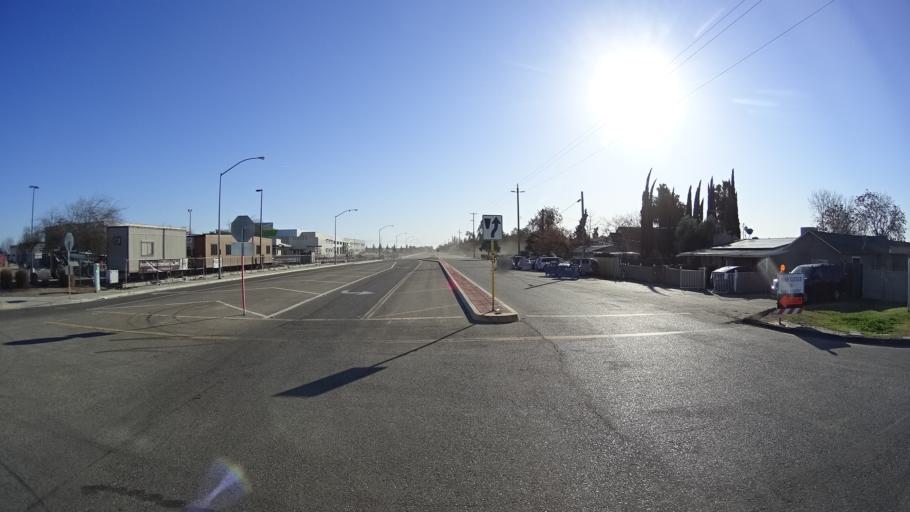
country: US
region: California
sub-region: Fresno County
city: Biola
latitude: 36.7934
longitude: -119.9164
